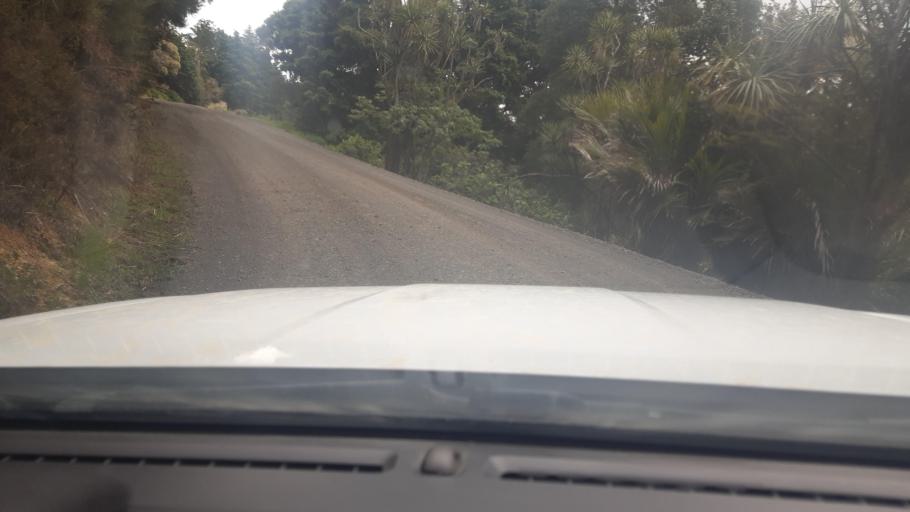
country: NZ
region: Northland
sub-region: Far North District
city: Kaitaia
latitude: -35.0657
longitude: 173.3287
